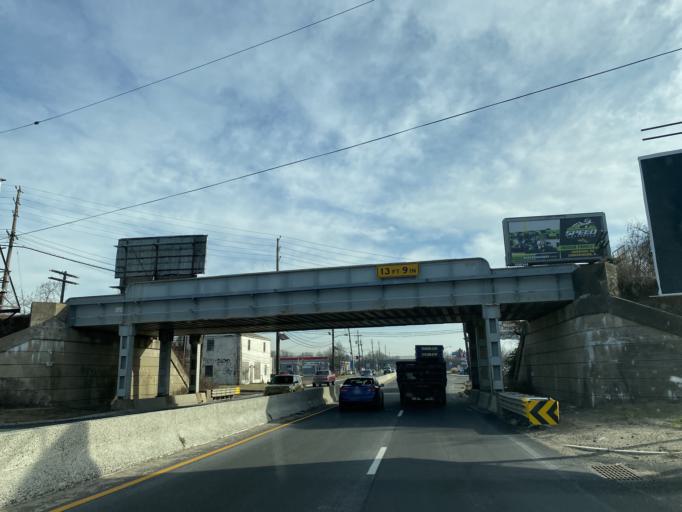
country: US
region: New Jersey
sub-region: Burlington County
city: Palmyra
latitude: 39.9972
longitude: -75.0338
